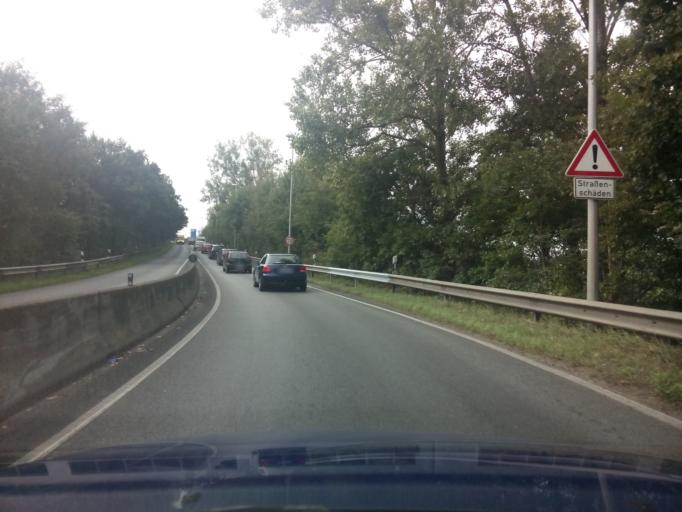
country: DE
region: Lower Saxony
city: Lilienthal
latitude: 53.1164
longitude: 8.8736
